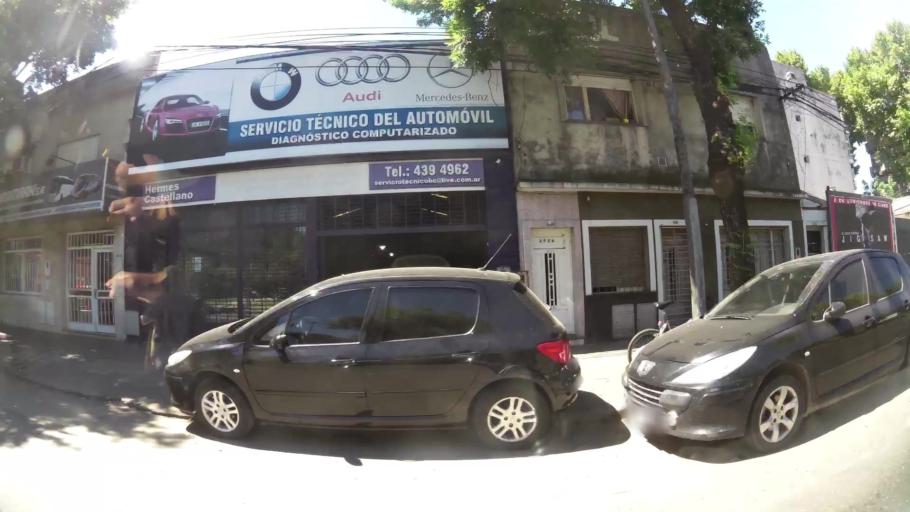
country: AR
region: Santa Fe
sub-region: Departamento de Rosario
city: Rosario
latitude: -32.9382
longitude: -60.6765
